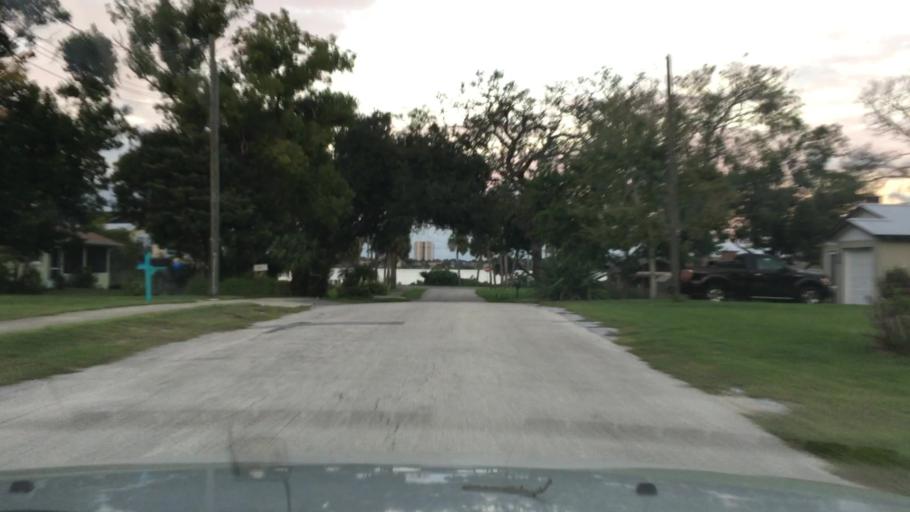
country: US
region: Florida
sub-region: Volusia County
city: Holly Hill
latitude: 29.2420
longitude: -81.0363
